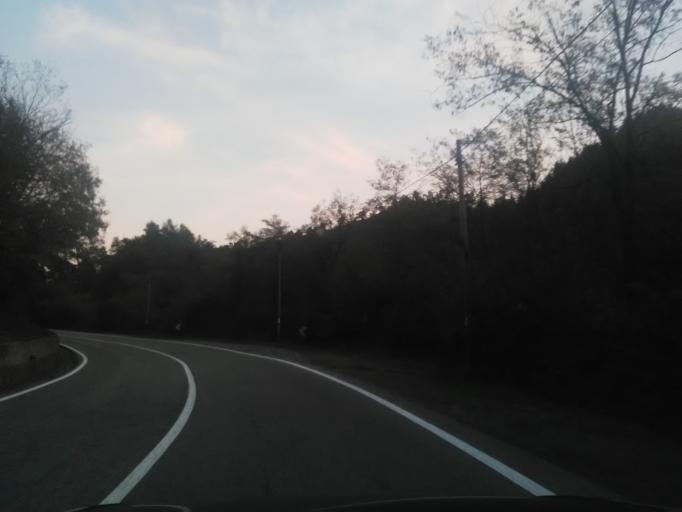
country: IT
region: Piedmont
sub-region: Provincia di Biella
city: Sostegno
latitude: 45.6692
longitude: 8.2584
